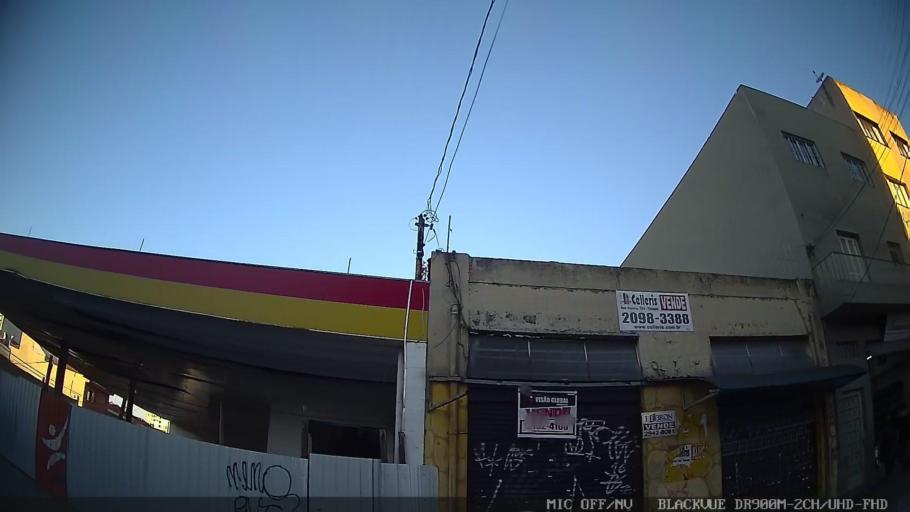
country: BR
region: Sao Paulo
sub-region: Sao Paulo
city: Sao Paulo
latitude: -23.5409
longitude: -46.5572
